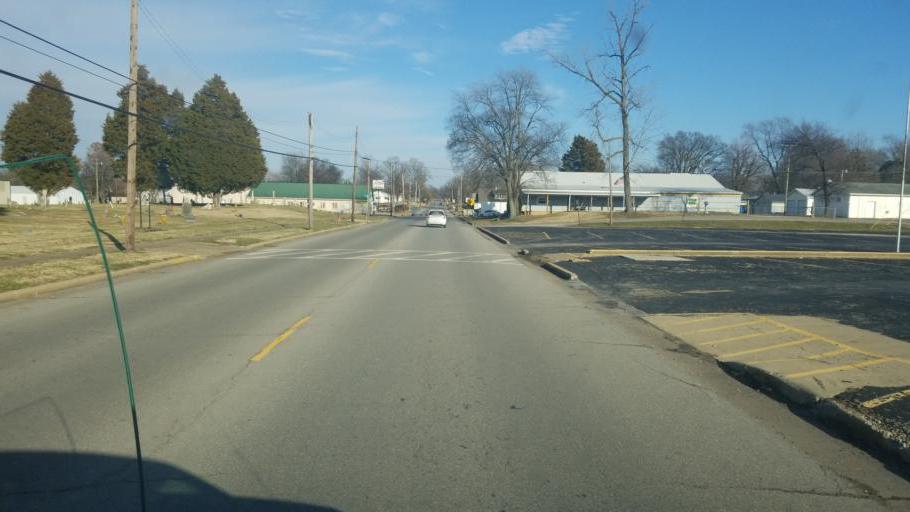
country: US
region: Illinois
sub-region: Wabash County
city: Mount Carmel
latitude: 38.4048
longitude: -87.7699
